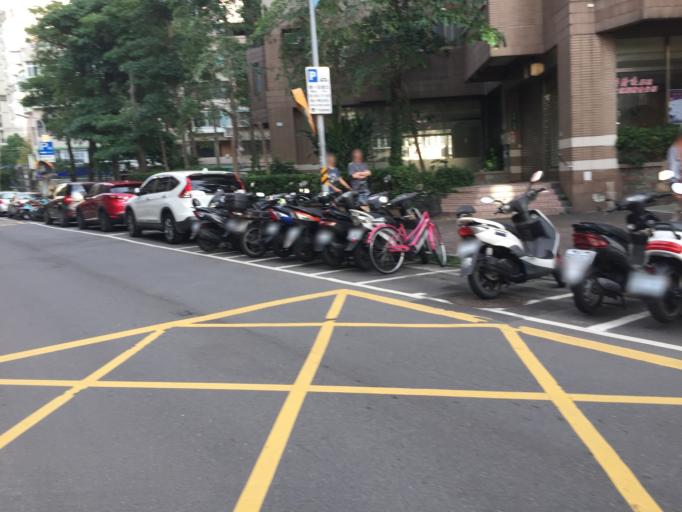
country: TW
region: Taipei
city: Taipei
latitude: 25.1086
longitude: 121.5330
